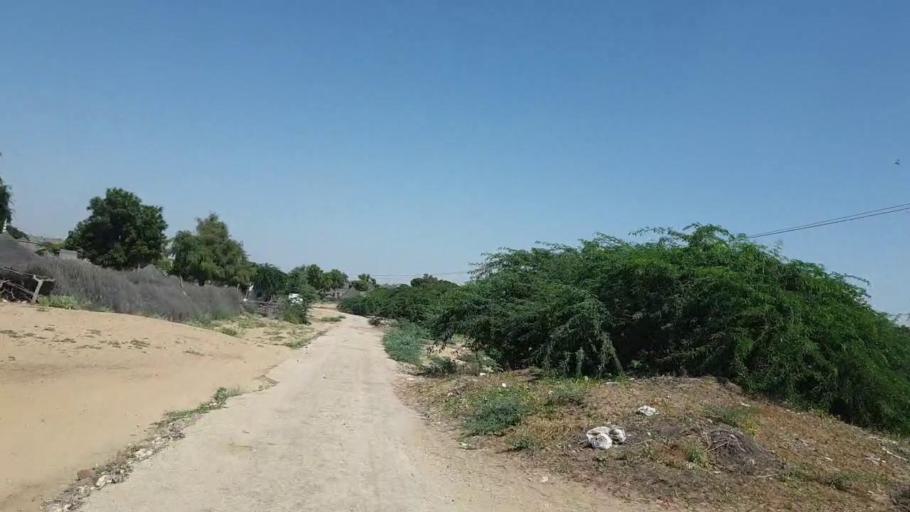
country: PK
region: Sindh
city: Islamkot
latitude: 25.1522
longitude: 70.4091
